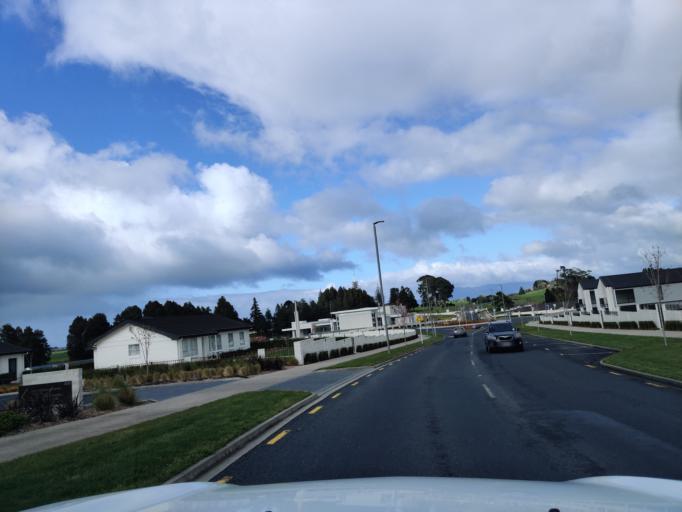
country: NZ
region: Waikato
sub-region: Hamilton City
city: Hamilton
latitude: -37.8212
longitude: 175.2267
